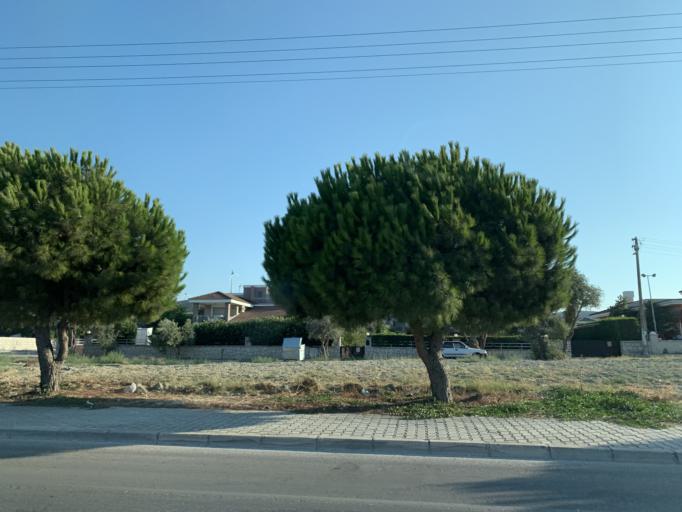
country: TR
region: Izmir
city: Alacati
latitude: 38.3084
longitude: 26.3530
